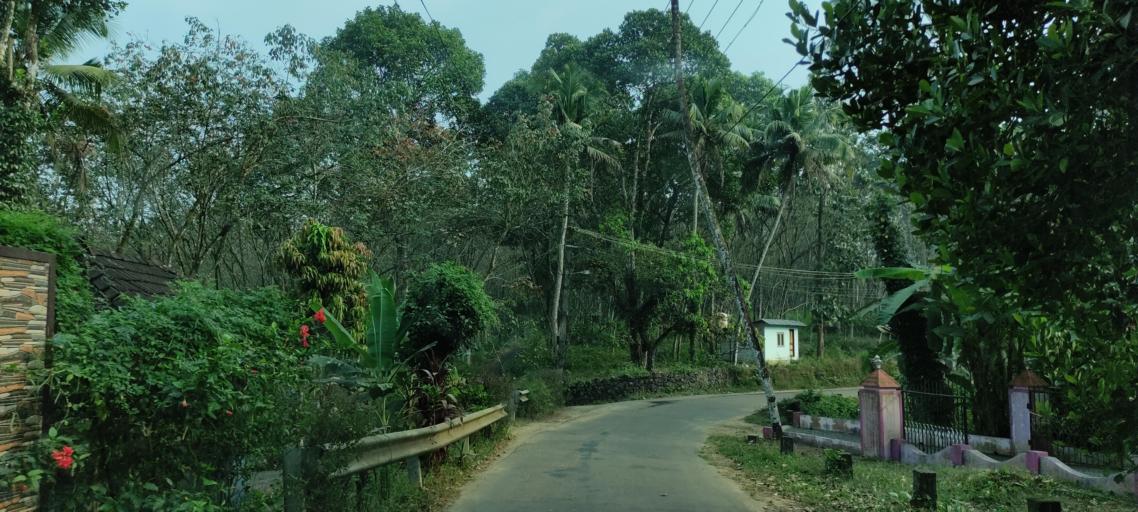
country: IN
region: Kerala
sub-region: Ernakulam
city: Piravam
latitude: 9.8071
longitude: 76.5357
